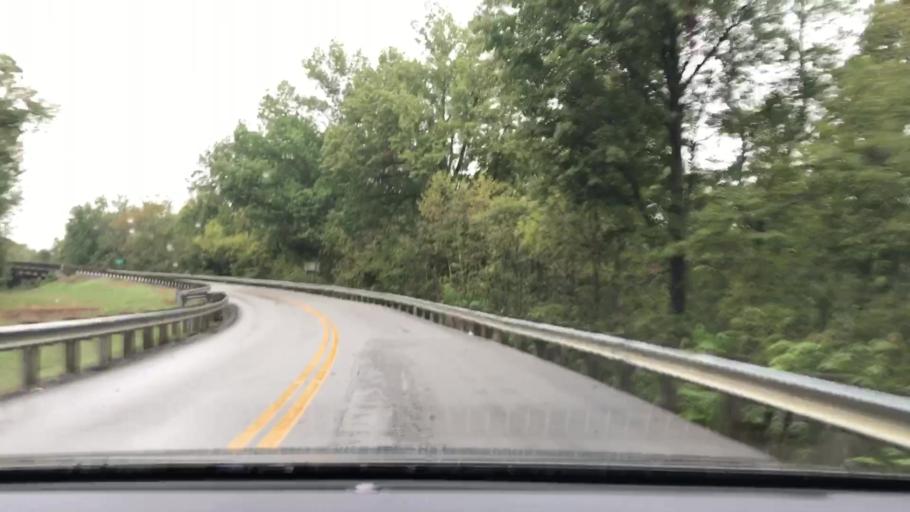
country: US
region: Kentucky
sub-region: McLean County
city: Calhoun
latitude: 37.3950
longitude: -87.3035
